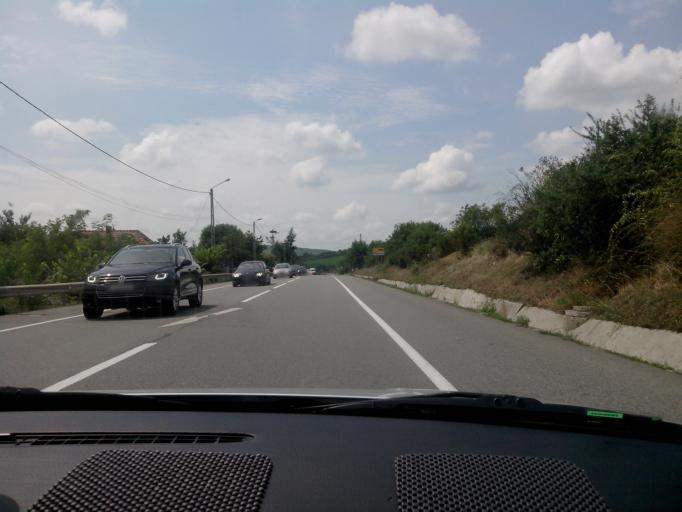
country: RO
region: Cluj
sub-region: Comuna Bontida
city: Rascruci
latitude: 46.9158
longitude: 23.7793
